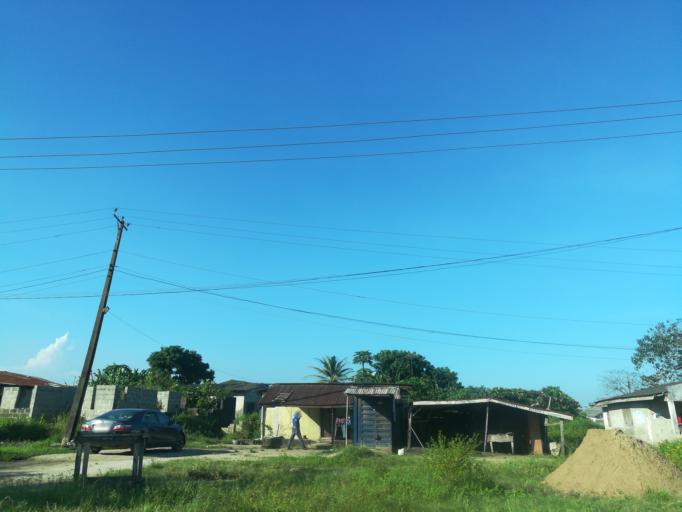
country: NG
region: Lagos
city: Ebute Ikorodu
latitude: 6.5412
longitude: 3.5478
